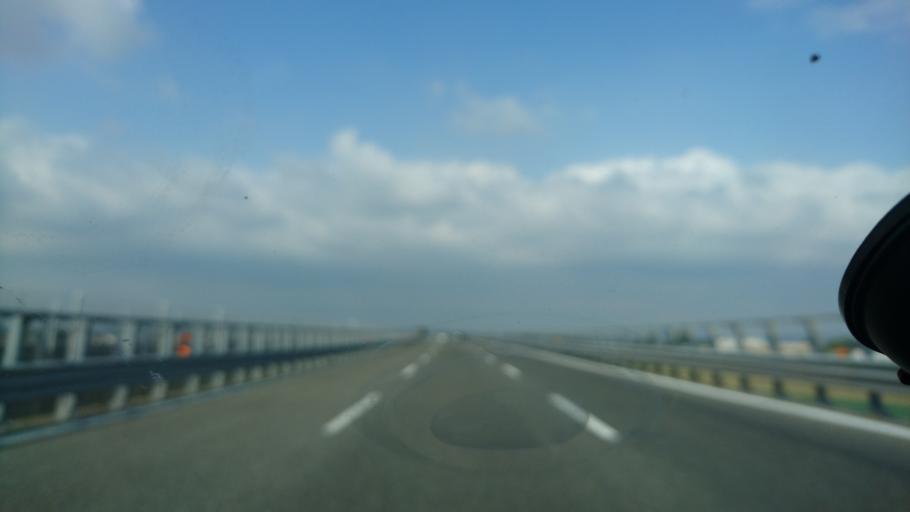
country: IT
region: Piedmont
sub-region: Provincia di Alessandria
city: Alessandria
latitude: 44.9169
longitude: 8.5775
